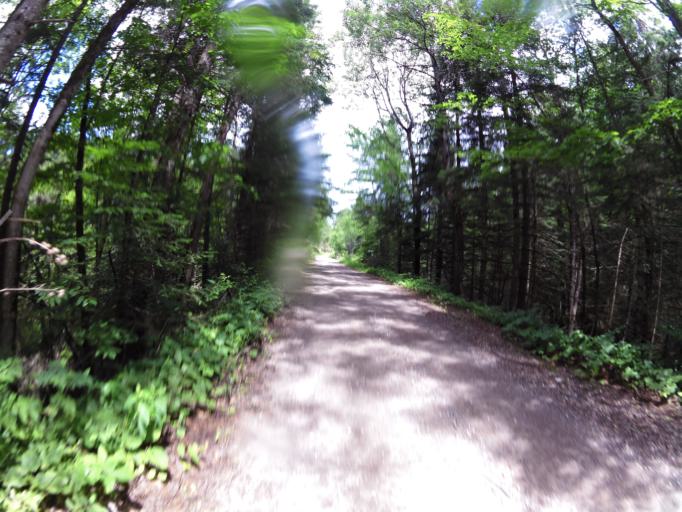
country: CA
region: Ontario
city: Renfrew
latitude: 45.0959
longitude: -76.7125
